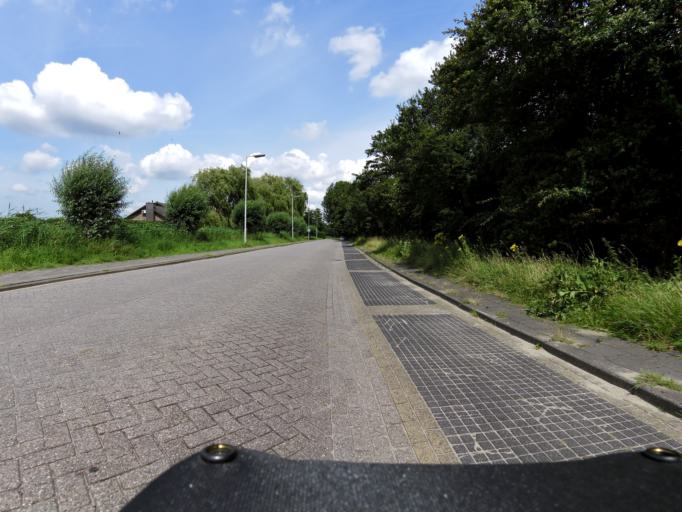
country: NL
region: South Holland
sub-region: Gemeente Albrandswaard
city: Rhoon
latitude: 51.8642
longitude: 4.4311
